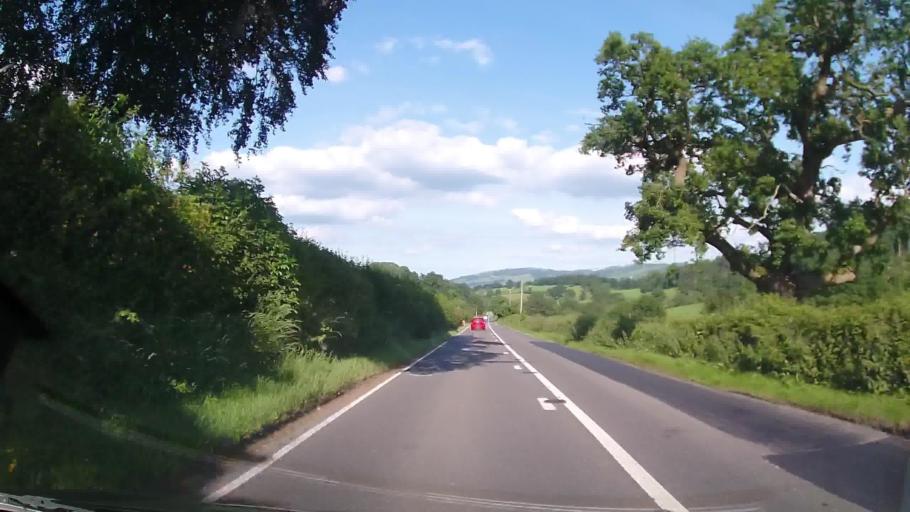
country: GB
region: Wales
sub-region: Sir Powys
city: Welshpool
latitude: 52.6547
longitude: -3.1802
